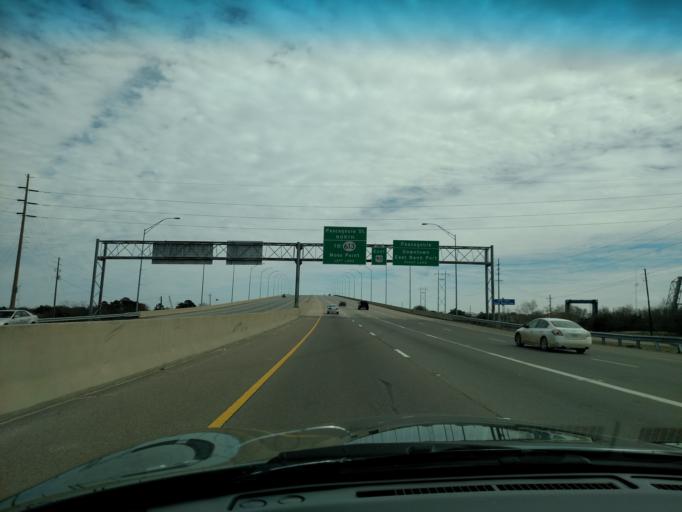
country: US
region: Mississippi
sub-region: Jackson County
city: Pascagoula
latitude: 30.3735
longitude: -88.5689
